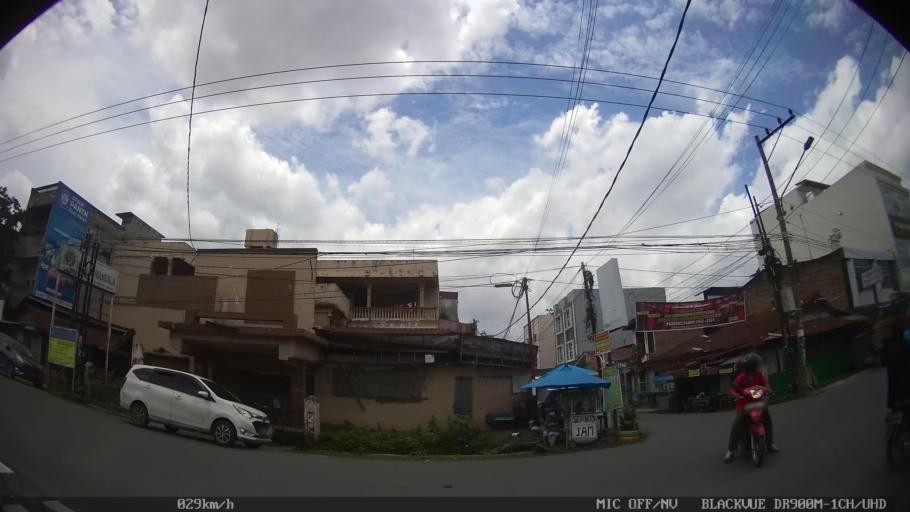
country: ID
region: North Sumatra
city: Medan
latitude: 3.5966
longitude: 98.7108
